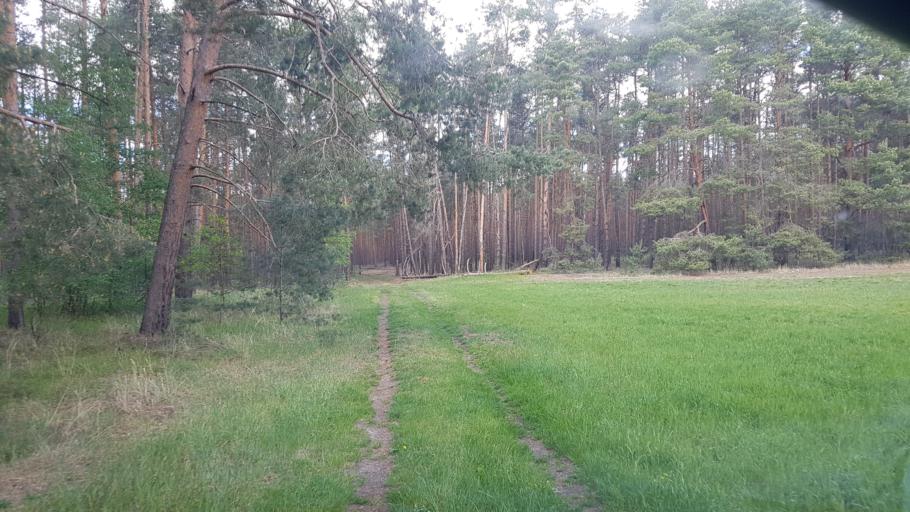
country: DE
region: Brandenburg
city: Finsterwalde
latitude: 51.6444
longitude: 13.6606
